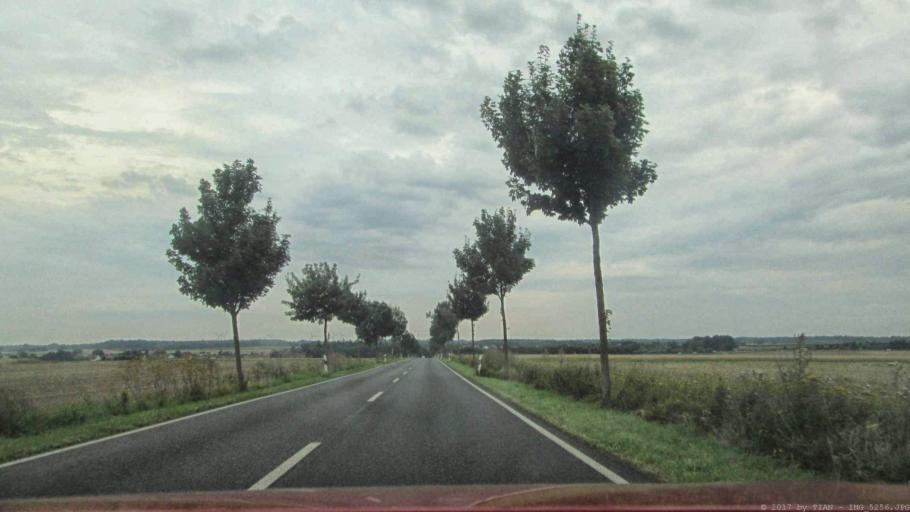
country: DE
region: Lower Saxony
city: Danndorf
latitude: 52.4028
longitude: 10.8488
